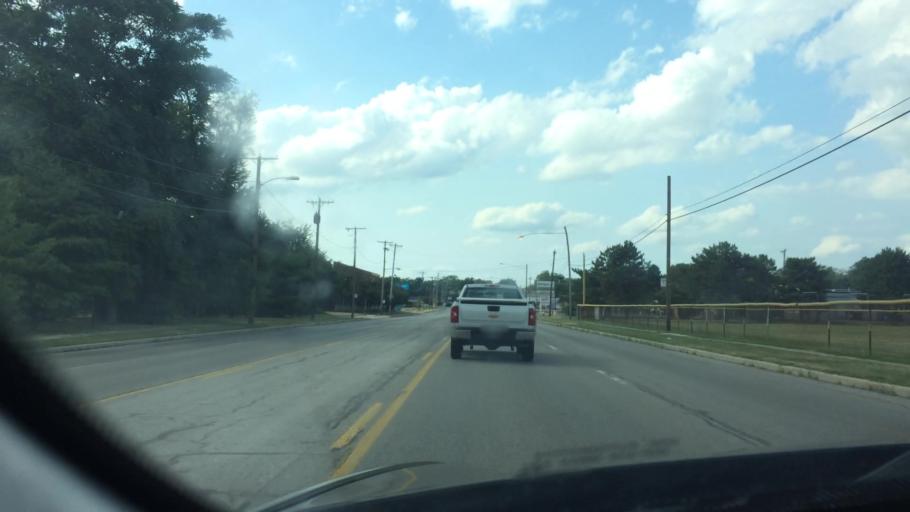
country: US
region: Ohio
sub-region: Wood County
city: Perrysburg
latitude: 41.5989
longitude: -83.6228
